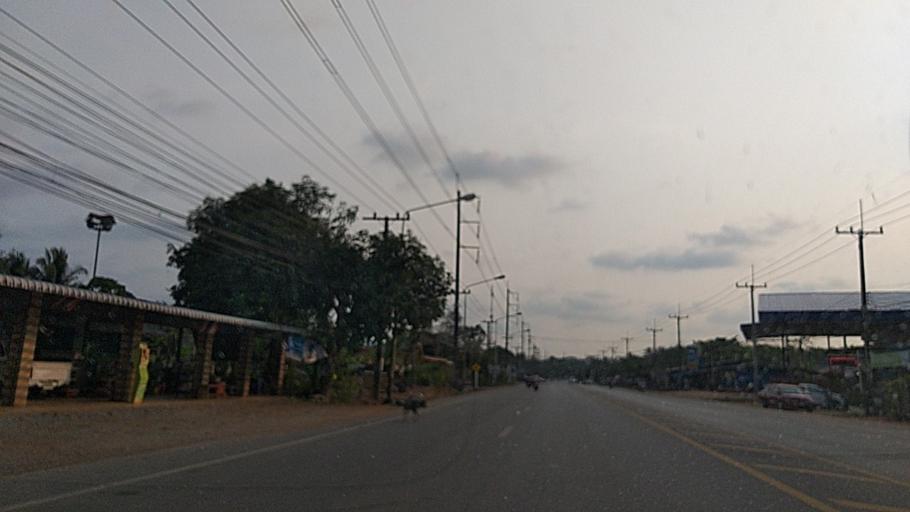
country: TH
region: Trat
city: Khao Saming
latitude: 12.3051
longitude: 102.3468
